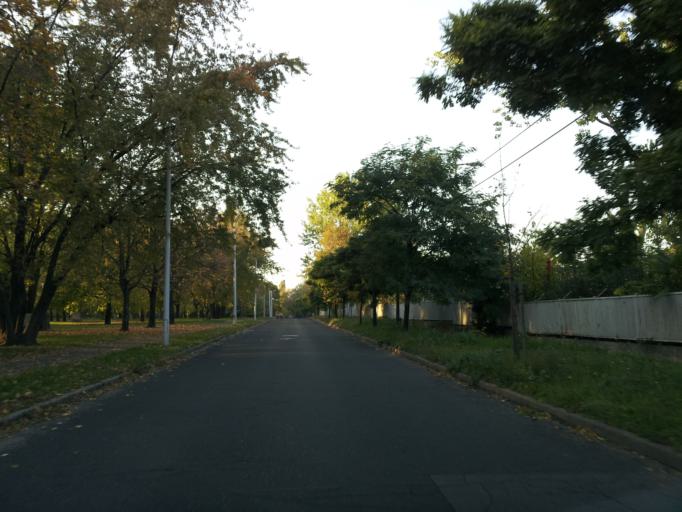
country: HU
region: Budapest
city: Budapest X. keruelet
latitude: 47.4856
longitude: 19.1465
